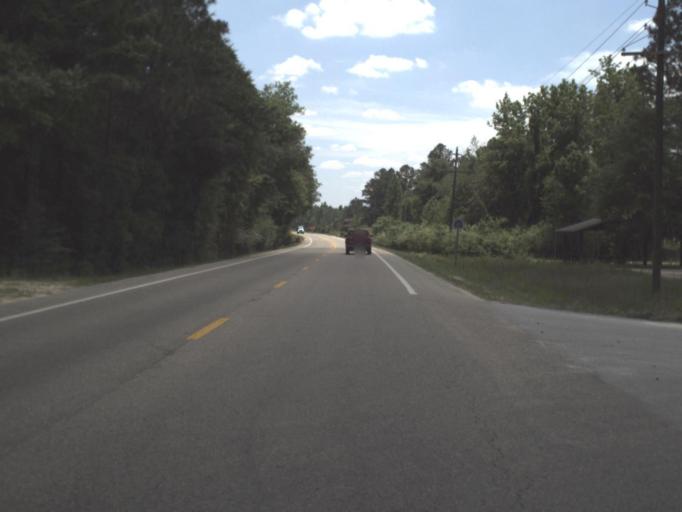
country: US
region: Florida
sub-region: Calhoun County
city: Blountstown
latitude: 30.4569
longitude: -85.0627
